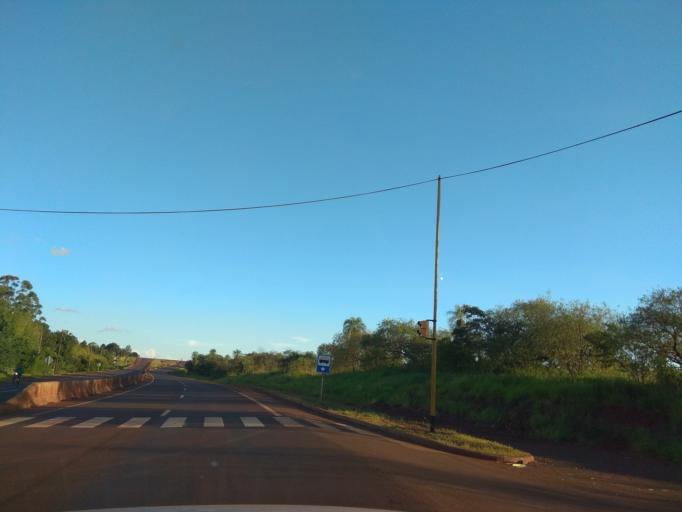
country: AR
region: Misiones
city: Garupa
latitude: -27.5282
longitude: -55.8580
